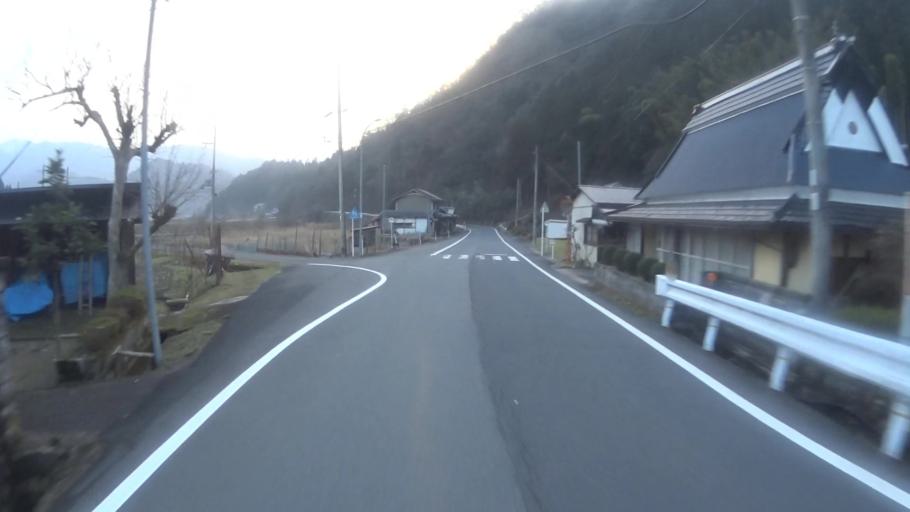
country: JP
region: Kyoto
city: Maizuru
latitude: 35.3786
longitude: 135.4453
